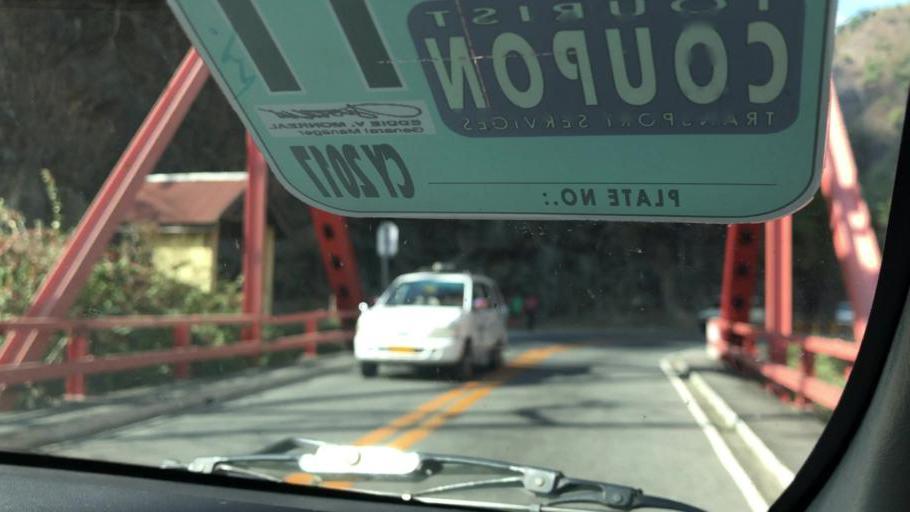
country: PH
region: Cordillera
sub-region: Province of Benguet
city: Tuba
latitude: 16.3206
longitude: 120.6148
